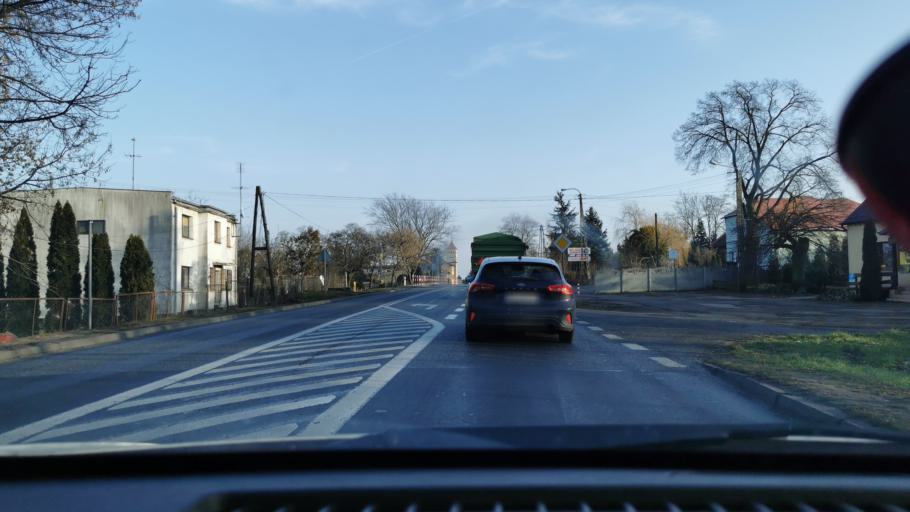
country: PL
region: Lodz Voivodeship
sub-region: Powiat sieradzki
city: Wroblew
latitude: 51.6123
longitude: 18.6143
